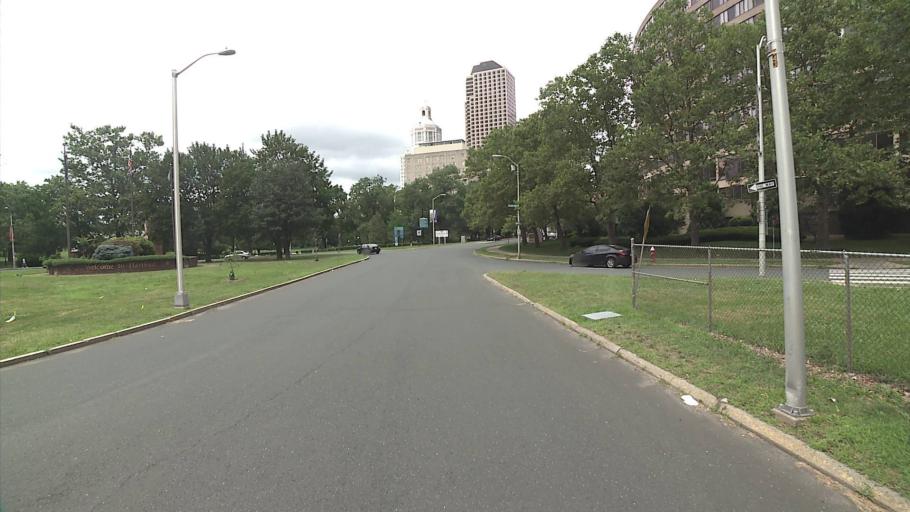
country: US
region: Connecticut
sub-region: Hartford County
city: Hartford
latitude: 41.7628
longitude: -72.6757
